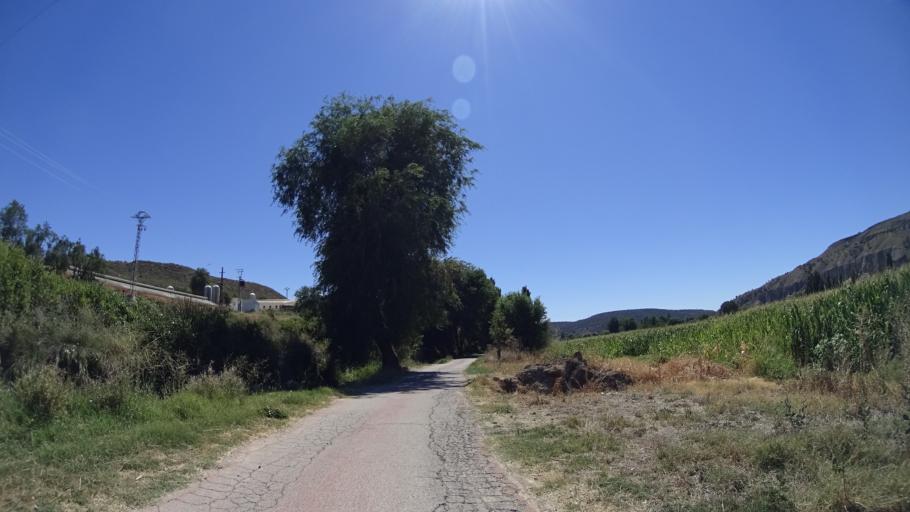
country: ES
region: Madrid
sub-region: Provincia de Madrid
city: Tielmes
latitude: 40.2328
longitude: -3.3234
